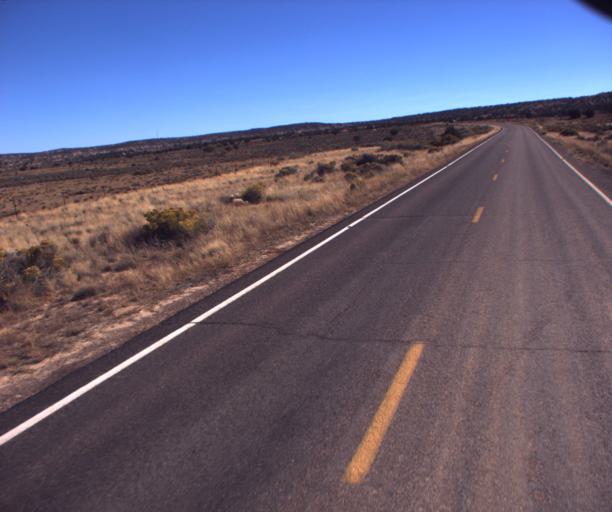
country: US
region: Arizona
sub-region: Navajo County
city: First Mesa
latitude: 35.7516
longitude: -110.1323
